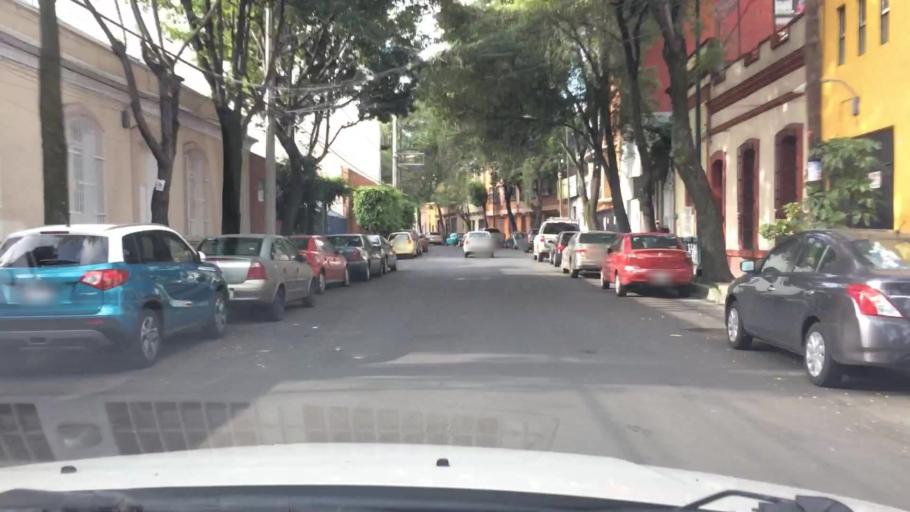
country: MX
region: Mexico City
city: Polanco
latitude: 19.4048
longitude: -99.1815
